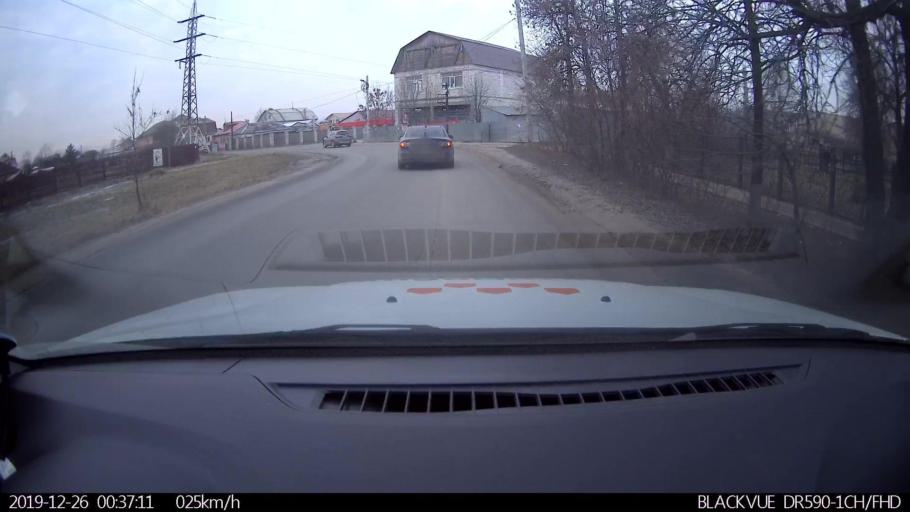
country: RU
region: Nizjnij Novgorod
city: Nizhniy Novgorod
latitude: 56.2899
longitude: 43.9039
